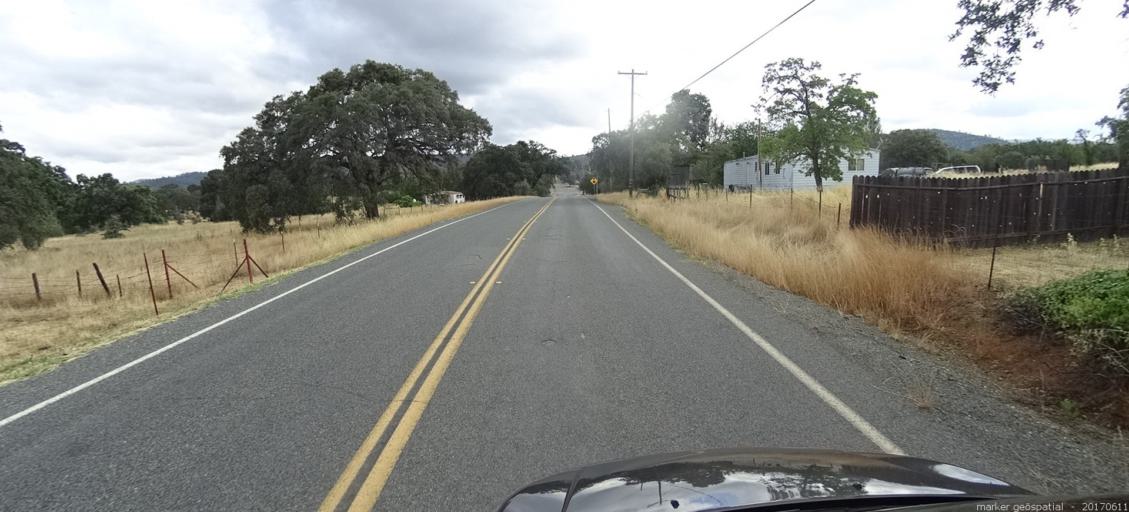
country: US
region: California
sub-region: Yuba County
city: Loma Rica
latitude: 39.3862
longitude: -121.4079
